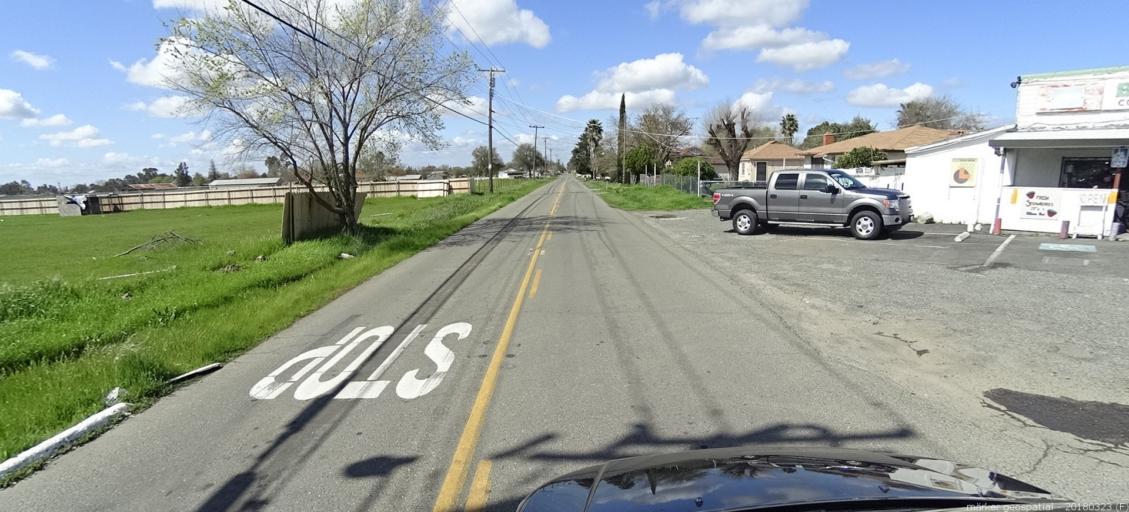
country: US
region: California
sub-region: Sacramento County
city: North Highlands
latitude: 38.6834
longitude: -121.4107
